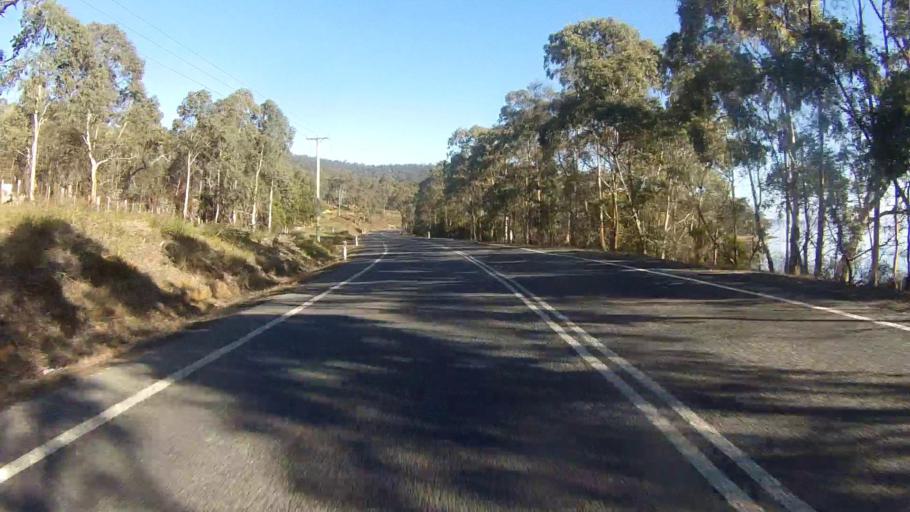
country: AU
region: Tasmania
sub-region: Clarence
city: Sandford
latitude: -43.0215
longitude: 147.8993
